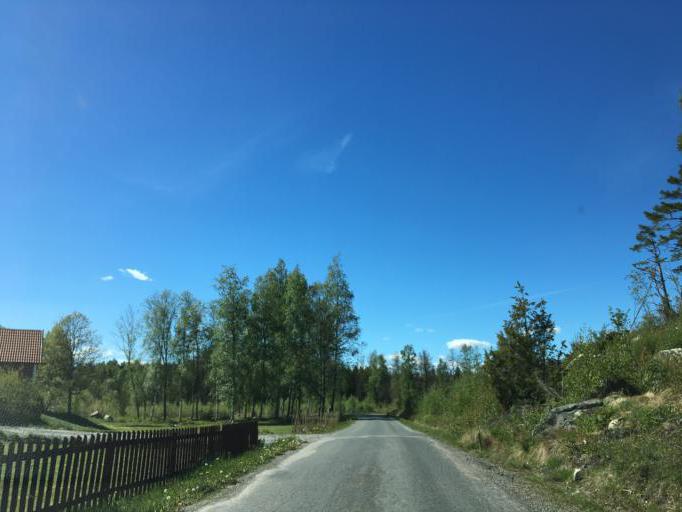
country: SE
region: Soedermanland
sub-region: Eskilstuna Kommun
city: Hallbybrunn
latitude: 59.3535
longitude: 16.3682
